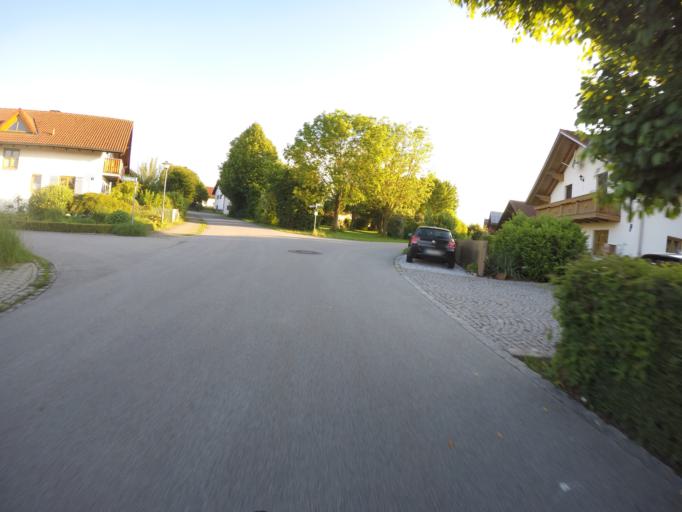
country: DE
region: Bavaria
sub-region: Lower Bavaria
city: Reisbach
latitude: 48.5709
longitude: 12.6213
